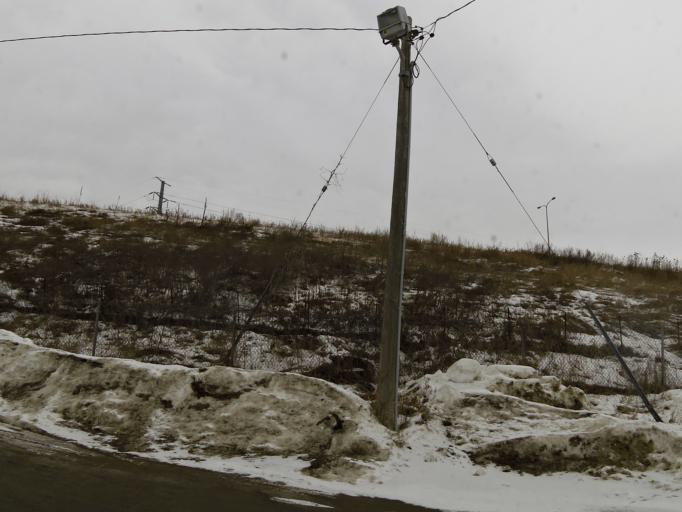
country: US
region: Minnesota
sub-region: Dakota County
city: South Saint Paul
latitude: 44.8777
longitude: -93.0272
